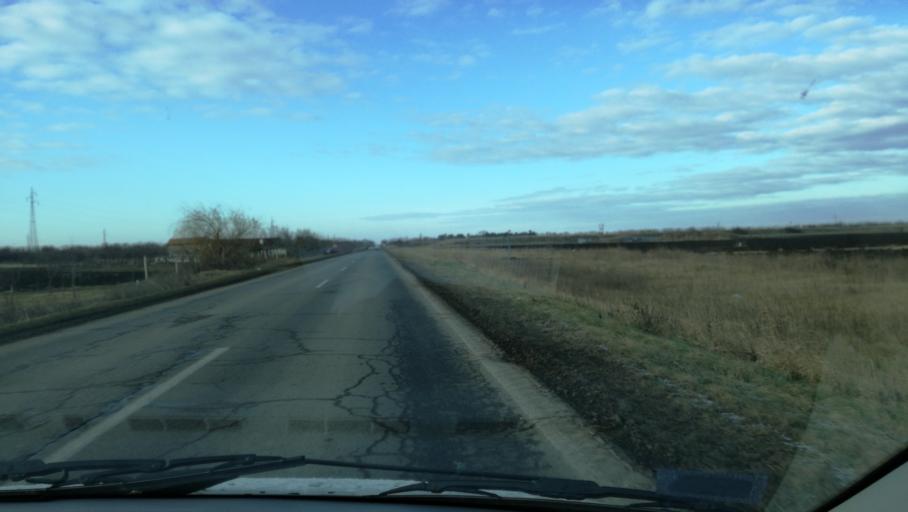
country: RS
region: Autonomna Pokrajina Vojvodina
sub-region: Severnobanatski Okrug
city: Kikinda
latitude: 45.8229
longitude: 20.4227
